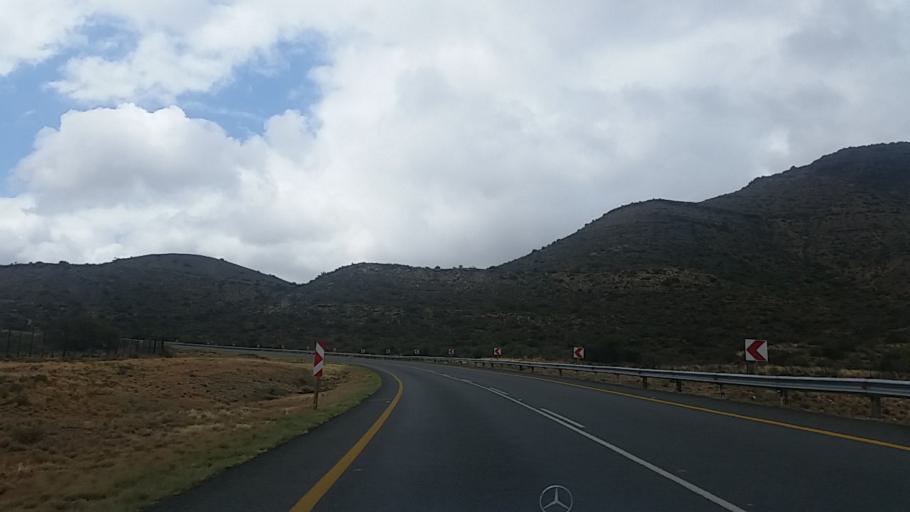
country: ZA
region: Eastern Cape
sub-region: Cacadu District Municipality
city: Graaff-Reinet
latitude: -32.1190
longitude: 24.6068
